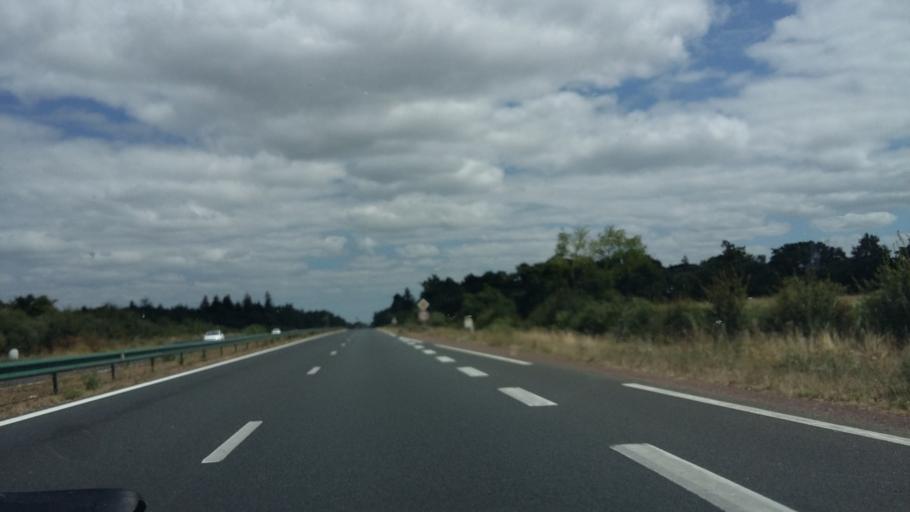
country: FR
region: Pays de la Loire
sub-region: Departement de la Vendee
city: Bournezeau
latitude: 46.6515
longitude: -1.2256
